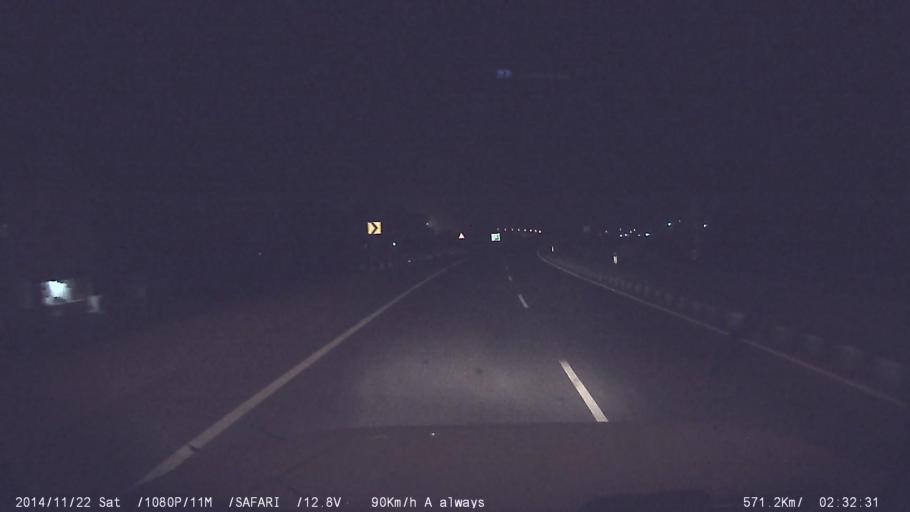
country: IN
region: Tamil Nadu
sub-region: Salem
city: Belur
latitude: 11.6574
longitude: 78.4207
